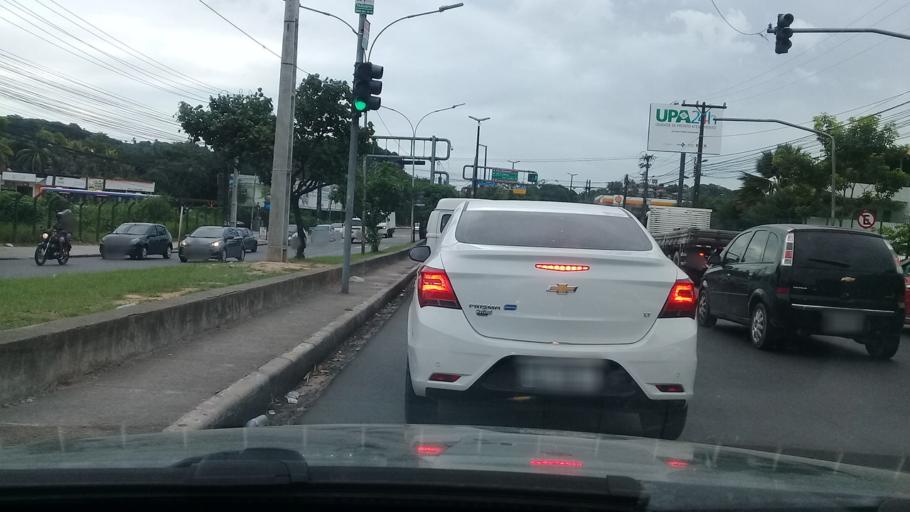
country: BR
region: Pernambuco
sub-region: Sao Lourenco Da Mata
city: Sao Lourenco da Mata
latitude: -8.0304
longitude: -34.9573
